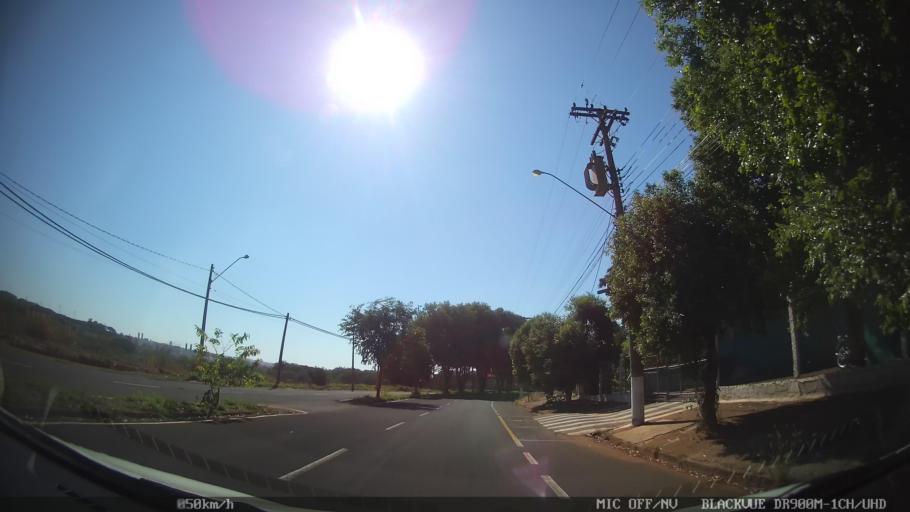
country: BR
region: Sao Paulo
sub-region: Sao Jose Do Rio Preto
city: Sao Jose do Rio Preto
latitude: -20.8131
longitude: -49.4297
